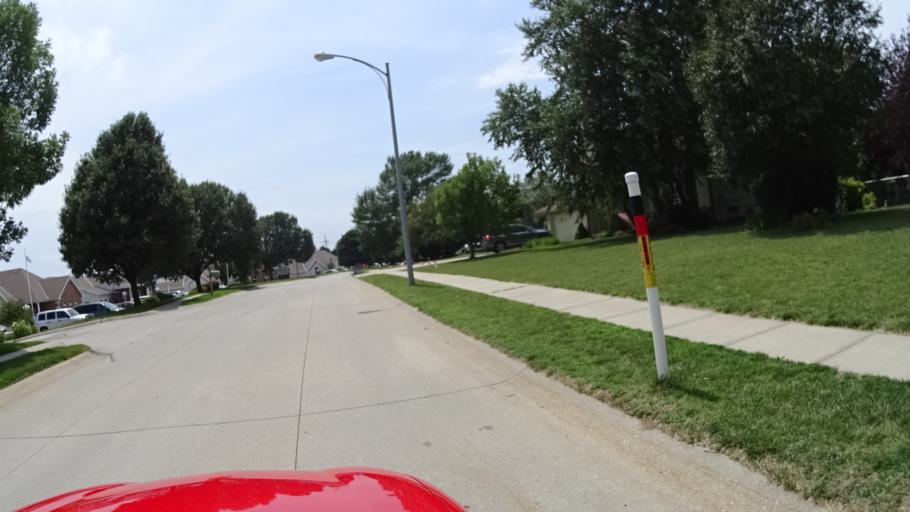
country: US
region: Nebraska
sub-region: Sarpy County
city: Papillion
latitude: 41.1420
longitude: -95.9840
